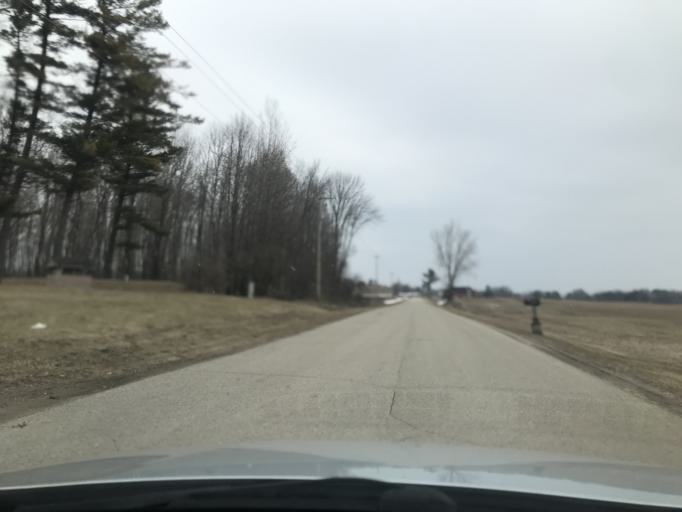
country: US
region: Wisconsin
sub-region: Marinette County
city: Peshtigo
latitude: 45.0436
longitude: -87.8558
